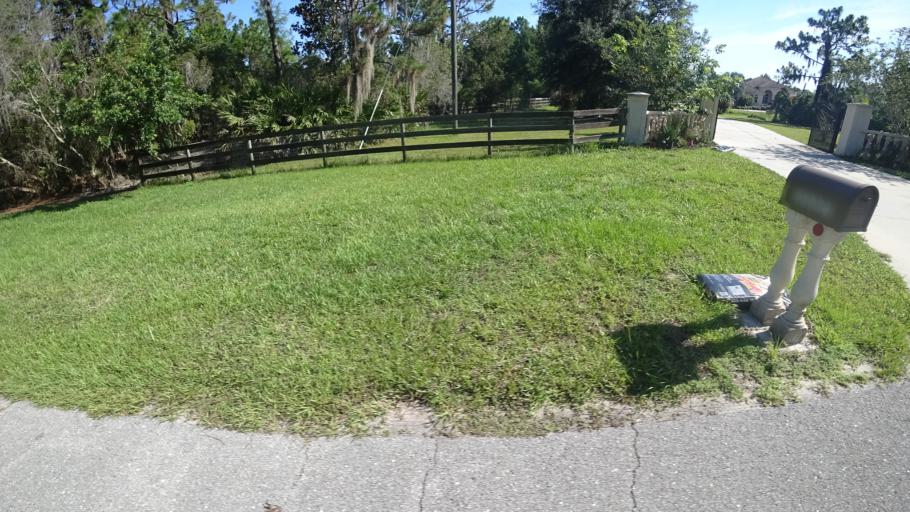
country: US
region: Florida
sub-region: Sarasota County
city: The Meadows
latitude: 27.4133
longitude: -82.3361
